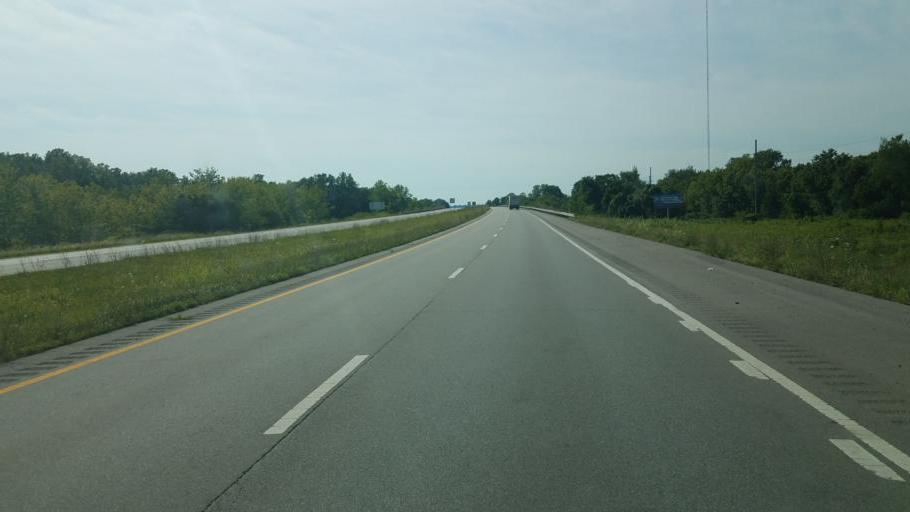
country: US
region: Ohio
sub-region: Hocking County
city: Logan
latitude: 39.5255
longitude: -82.3815
